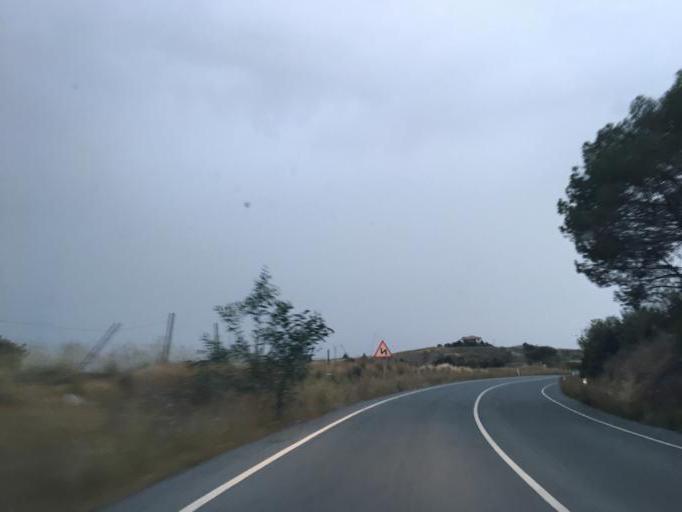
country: CY
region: Limassol
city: Parekklisha
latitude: 34.7675
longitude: 33.1634
